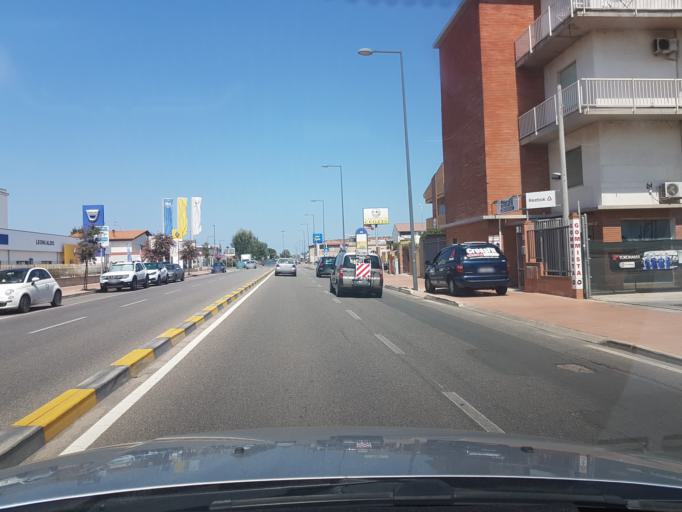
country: IT
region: Sardinia
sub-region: Provincia di Oristano
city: Oristano
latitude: 39.9132
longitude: 8.5866
